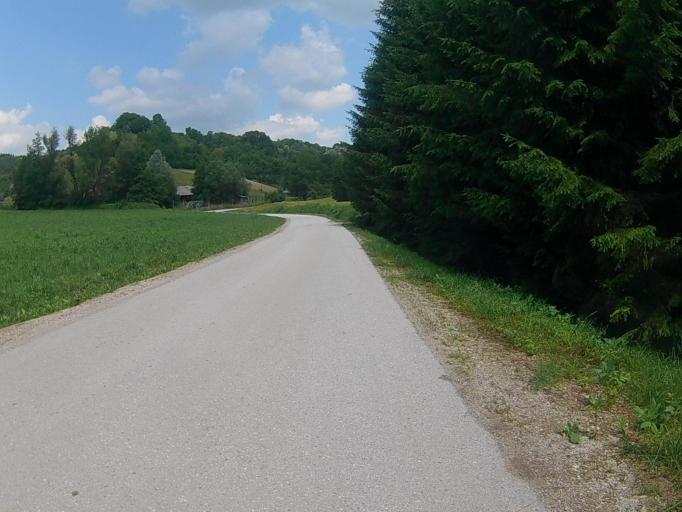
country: SI
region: Kungota
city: Zgornja Kungota
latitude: 46.6118
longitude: 15.6259
